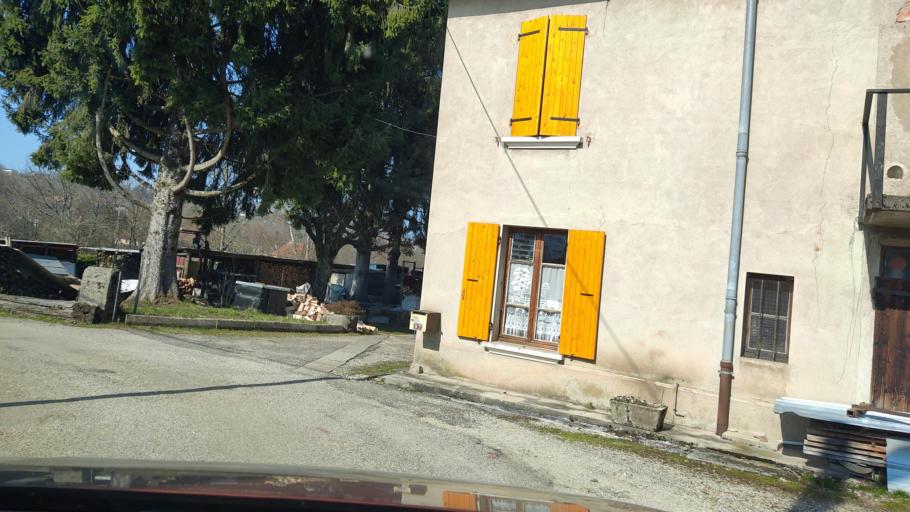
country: FR
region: Rhone-Alpes
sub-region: Departement de la Savoie
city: Saint-Beron
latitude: 45.5098
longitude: 5.7367
